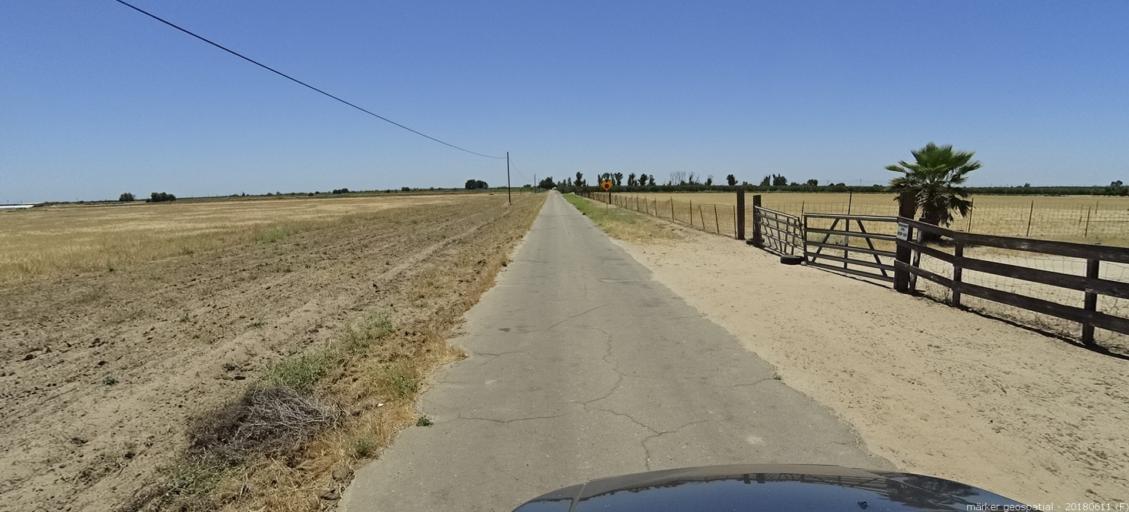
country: US
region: California
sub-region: Madera County
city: Fairmead
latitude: 37.0055
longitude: -120.1842
